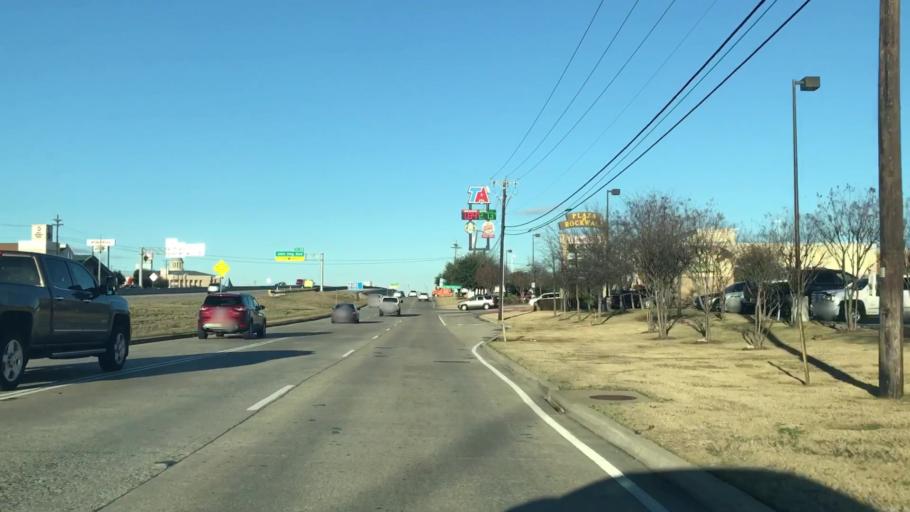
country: US
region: Texas
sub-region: Rockwall County
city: Rockwall
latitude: 32.9057
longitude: -96.4525
